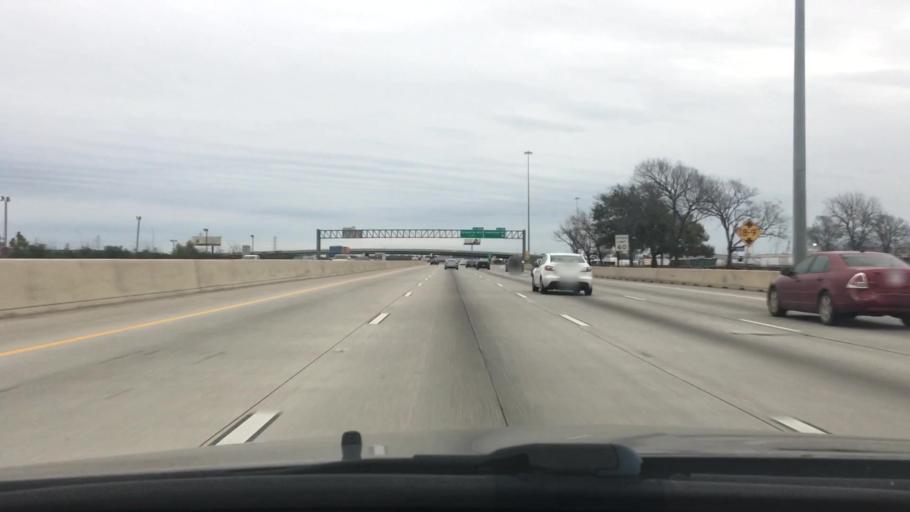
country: US
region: Texas
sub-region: Harris County
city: Houston
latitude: 29.8094
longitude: -95.3116
